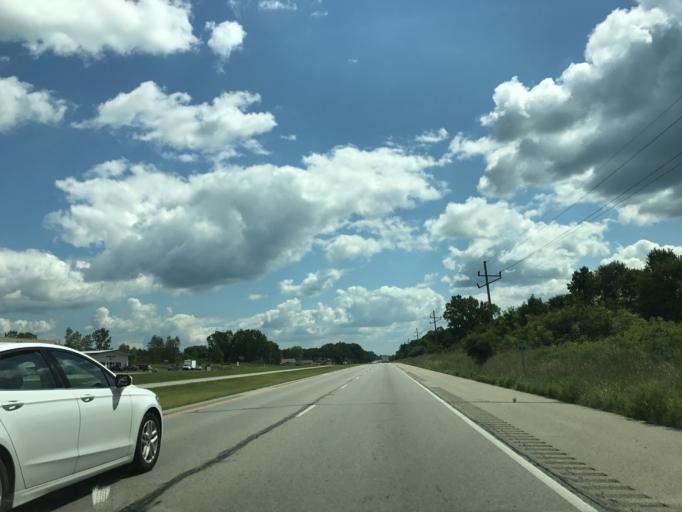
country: US
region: Indiana
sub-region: Kosciusko County
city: Winona Lake
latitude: 41.2193
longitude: -85.7739
